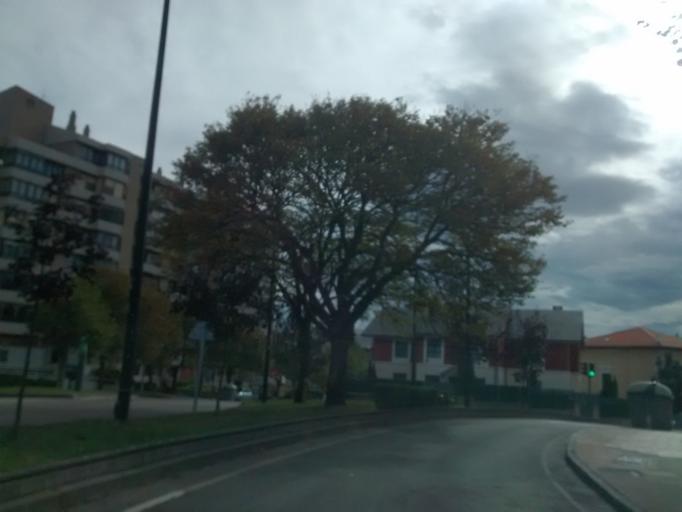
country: ES
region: Cantabria
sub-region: Provincia de Cantabria
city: Santander
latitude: 43.4609
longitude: -3.8302
